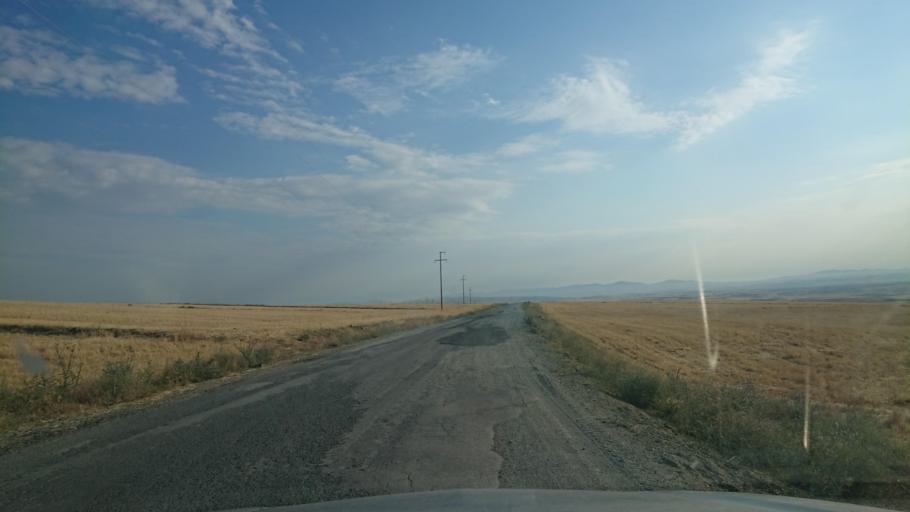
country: TR
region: Aksaray
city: Ortakoy
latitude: 38.7822
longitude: 34.0617
